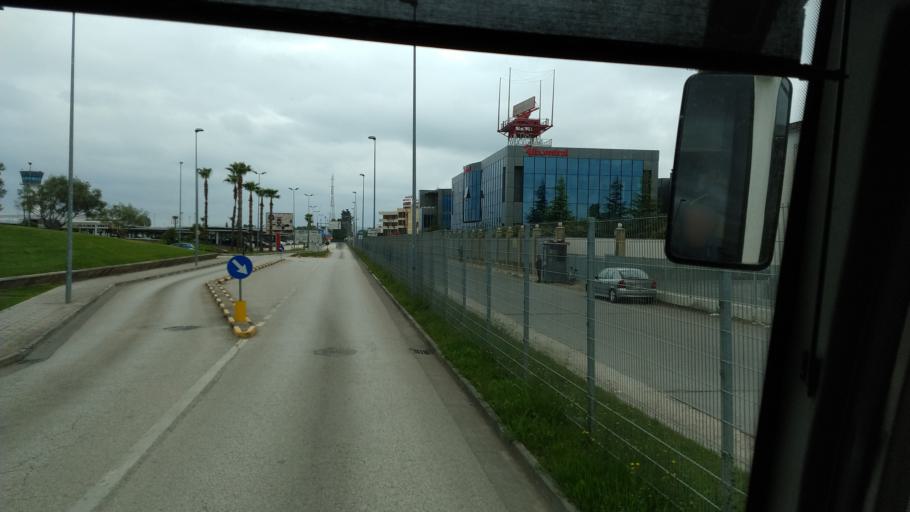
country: AL
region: Tirane
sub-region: Rrethi i Tiranes
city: Preze
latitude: 41.4193
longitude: 19.7126
